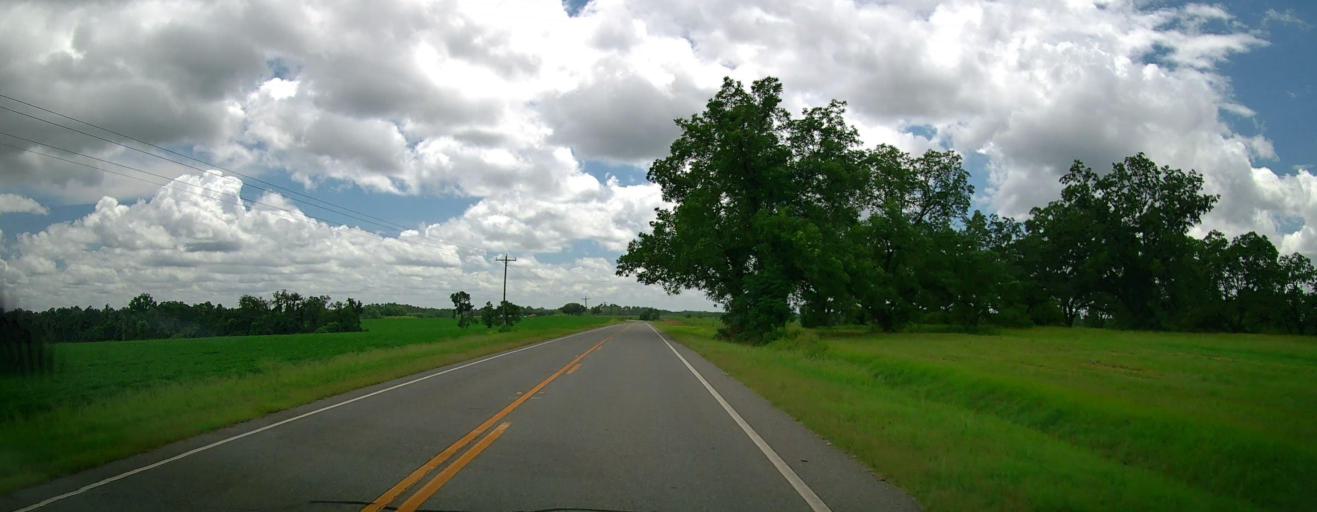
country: US
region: Georgia
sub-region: Wilcox County
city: Rochelle
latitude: 31.9774
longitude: -83.5462
